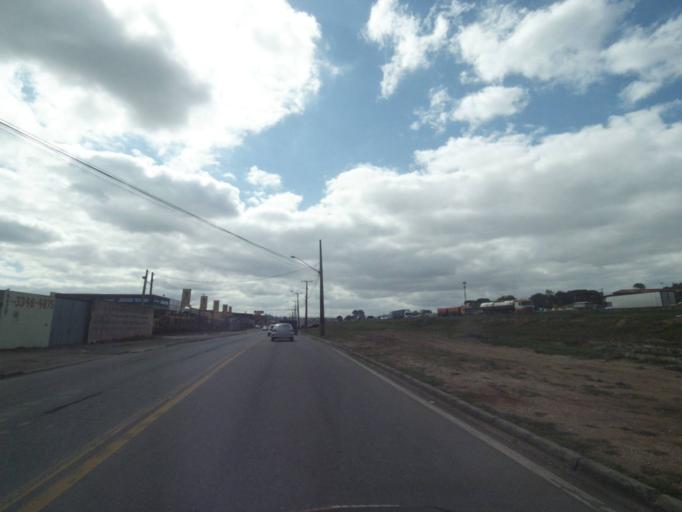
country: BR
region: Parana
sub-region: Sao Jose Dos Pinhais
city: Sao Jose dos Pinhais
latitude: -25.5536
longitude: -49.2772
